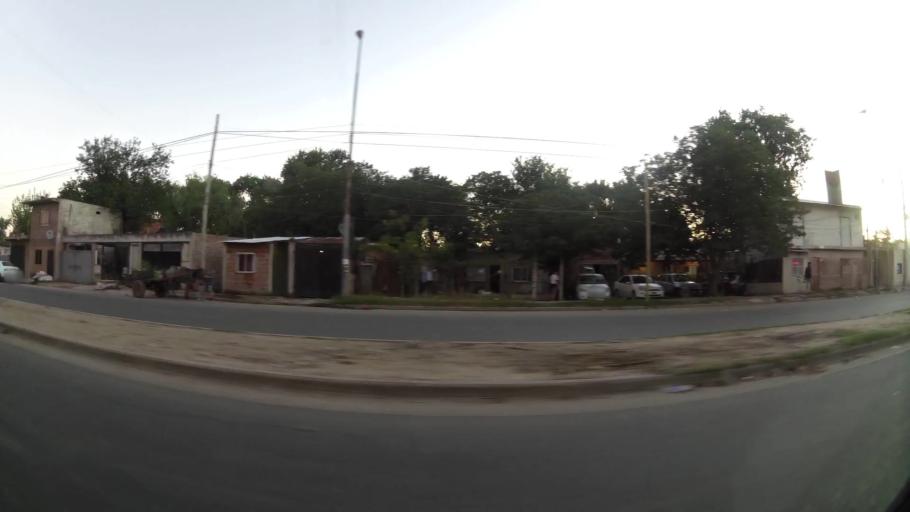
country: AR
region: Santa Fe
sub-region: Departamento de Rosario
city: Rosario
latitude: -32.9594
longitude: -60.6895
